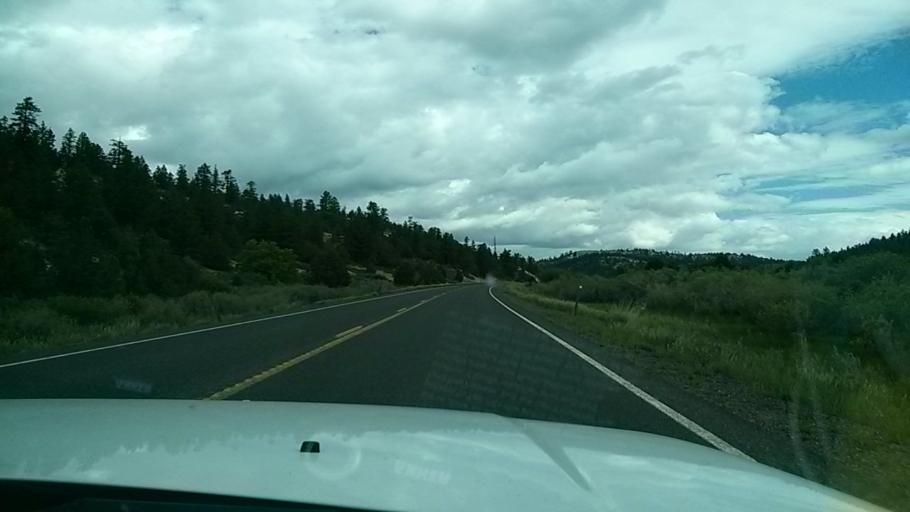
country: US
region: Utah
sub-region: Kane County
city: Kanab
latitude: 37.4301
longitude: -112.5384
